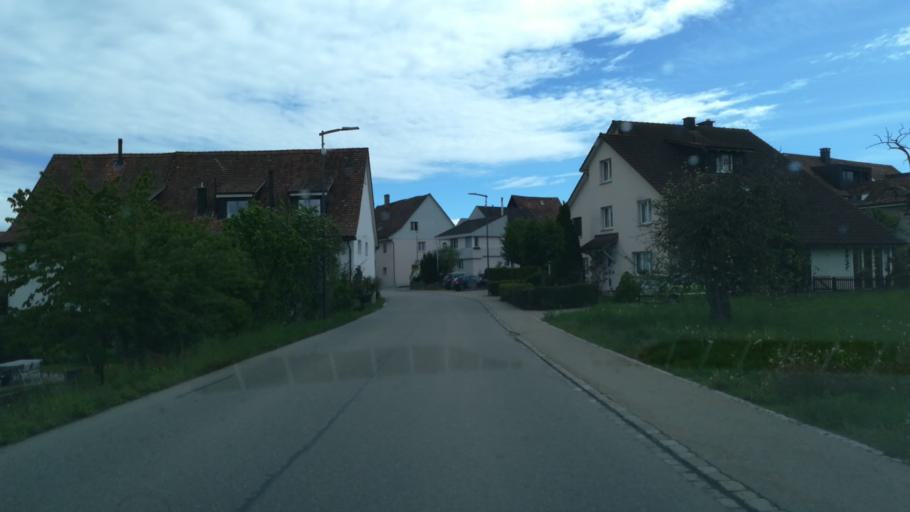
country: CH
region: Schaffhausen
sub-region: Bezirk Reiat
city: Stetten
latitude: 47.7412
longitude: 8.6631
